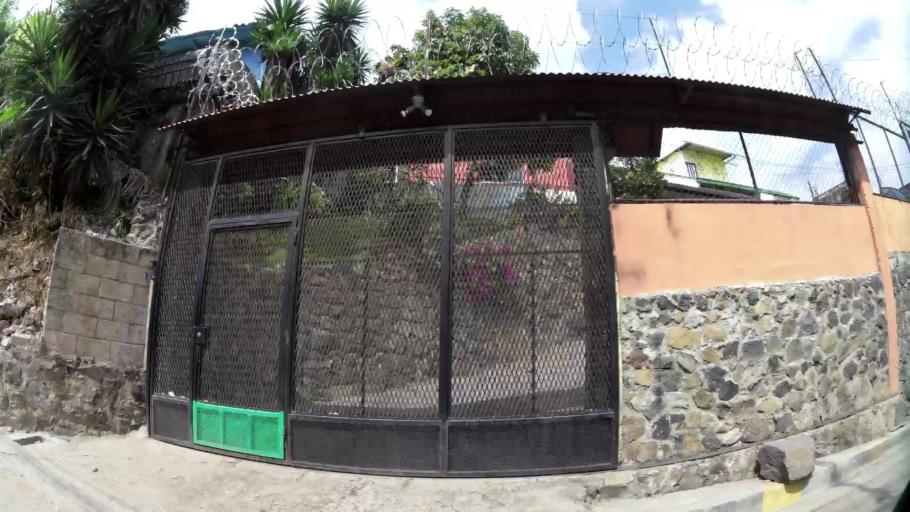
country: SV
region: San Salvador
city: Mejicanos
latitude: 13.7145
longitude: -89.2487
